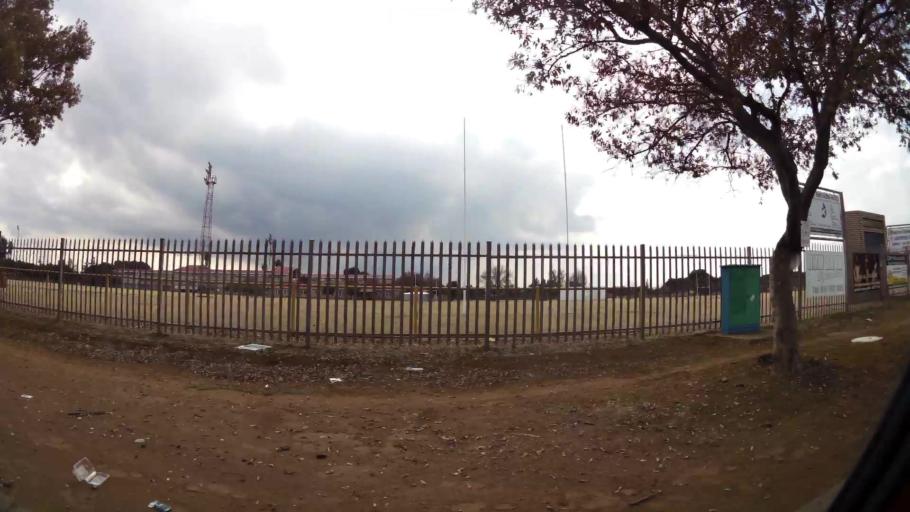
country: ZA
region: Gauteng
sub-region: Sedibeng District Municipality
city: Vanderbijlpark
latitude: -26.7249
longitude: 27.8476
